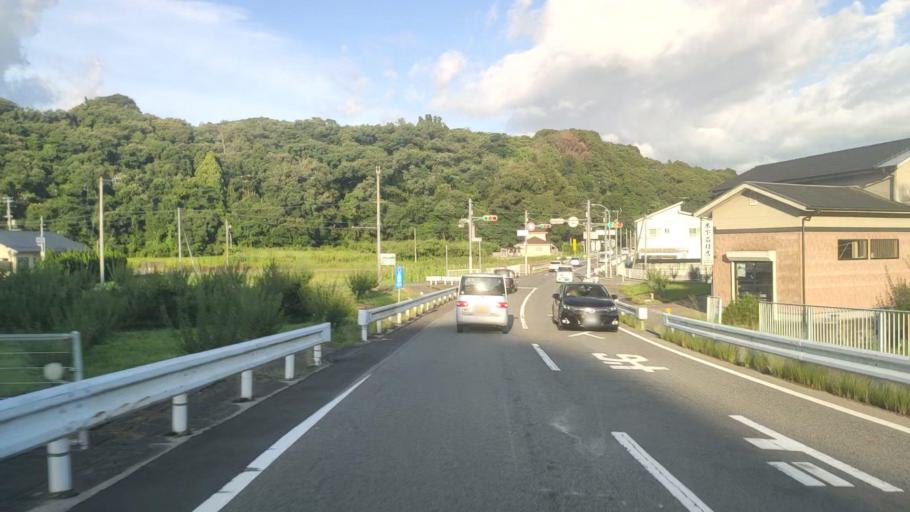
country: JP
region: Wakayama
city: Tanabe
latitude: 33.7267
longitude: 135.4415
